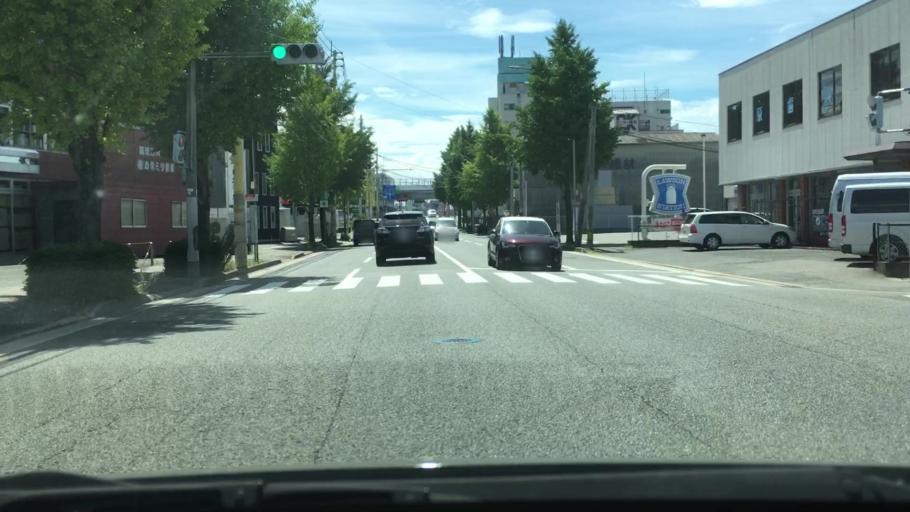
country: JP
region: Fukuoka
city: Onojo
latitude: 33.5574
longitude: 130.4516
